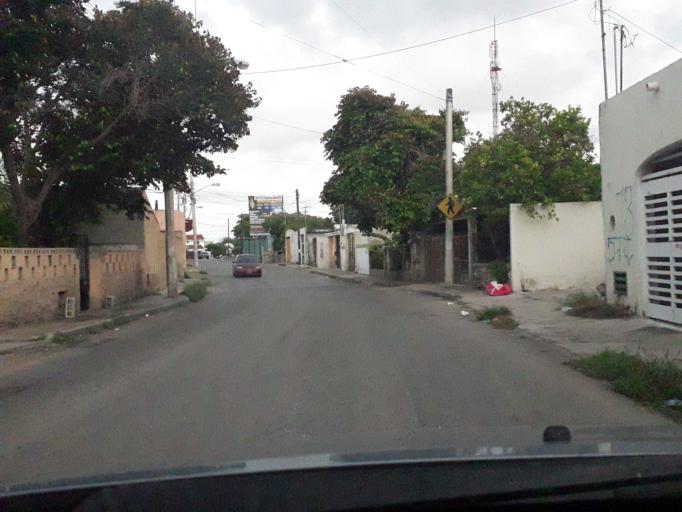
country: MX
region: Yucatan
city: Merida
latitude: 21.0203
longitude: -89.6372
